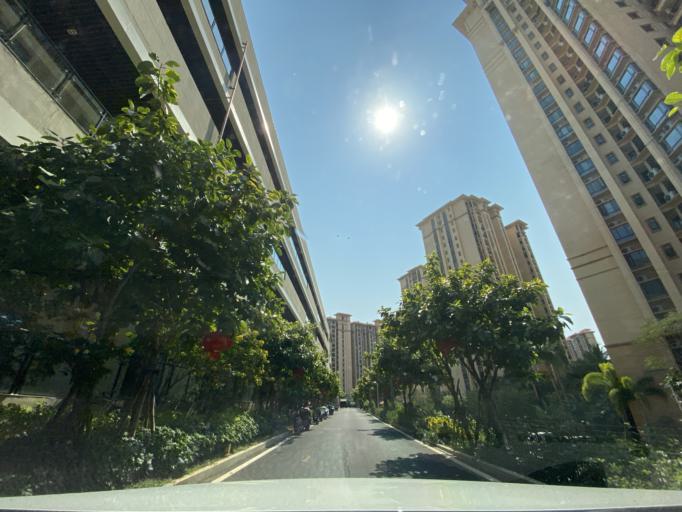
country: CN
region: Hainan
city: Yingzhou
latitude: 18.3987
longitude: 109.8405
